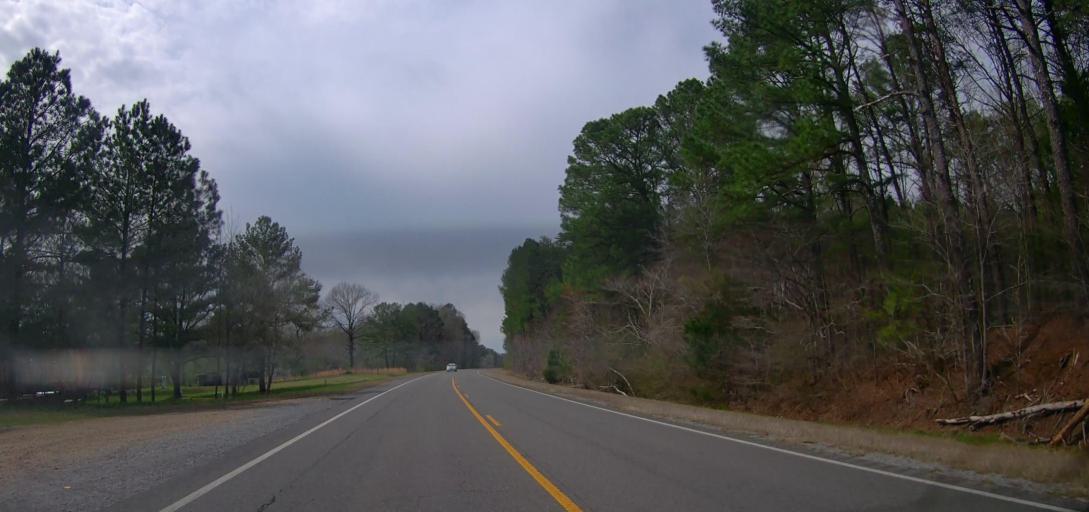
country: US
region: Alabama
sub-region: Walker County
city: Carbon Hill
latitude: 33.9021
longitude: -87.5472
